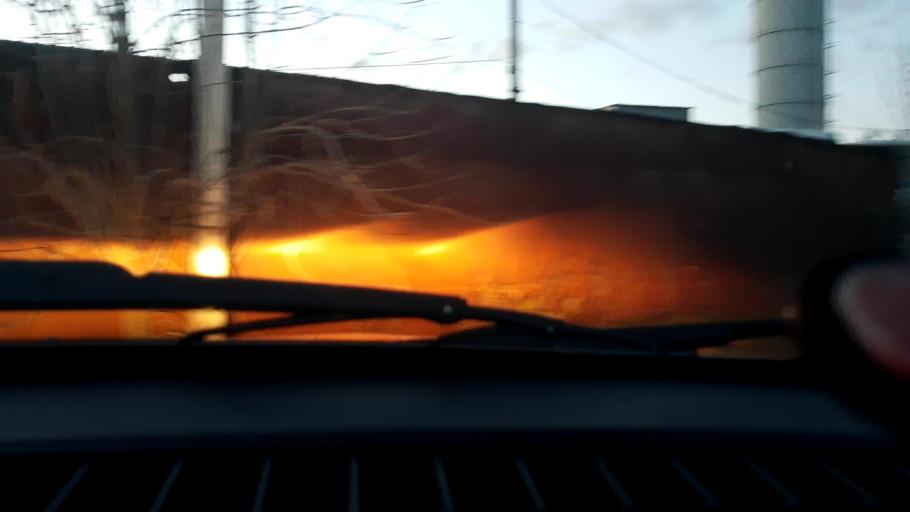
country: RU
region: Bashkortostan
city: Ufa
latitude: 54.7468
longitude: 55.9229
